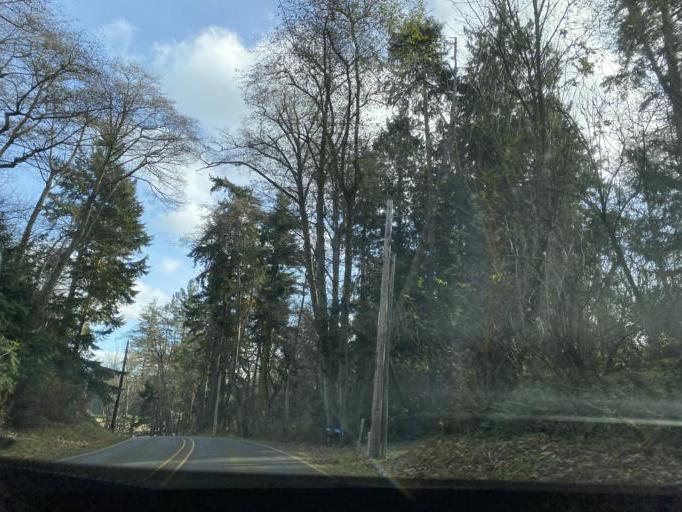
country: US
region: Washington
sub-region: Island County
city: Freeland
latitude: 47.9780
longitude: -122.4603
